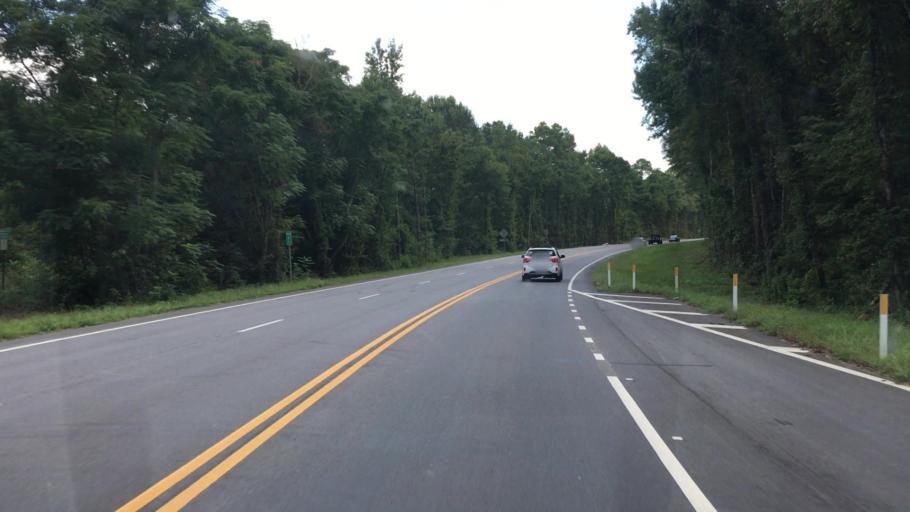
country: US
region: Georgia
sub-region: Putnam County
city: Jefferson
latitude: 33.4348
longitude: -83.3768
